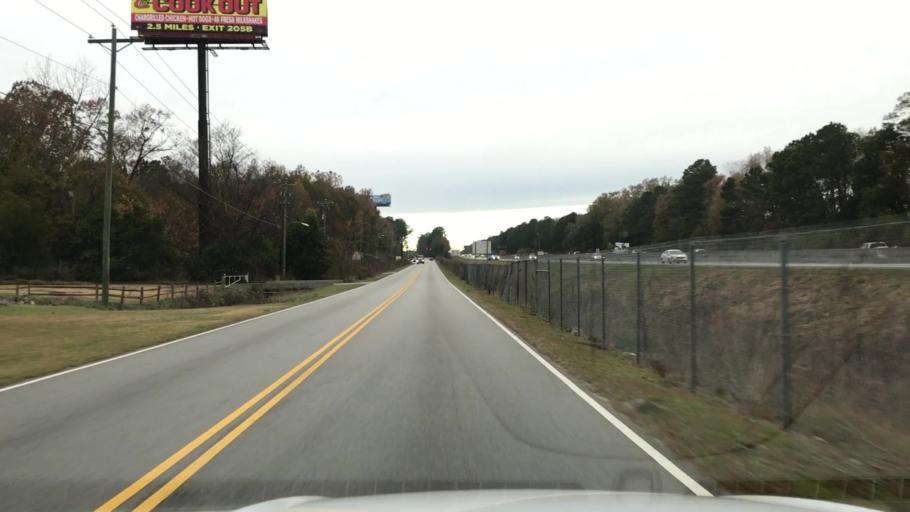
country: US
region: South Carolina
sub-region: Berkeley County
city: Goose Creek
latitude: 32.9453
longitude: -80.0553
